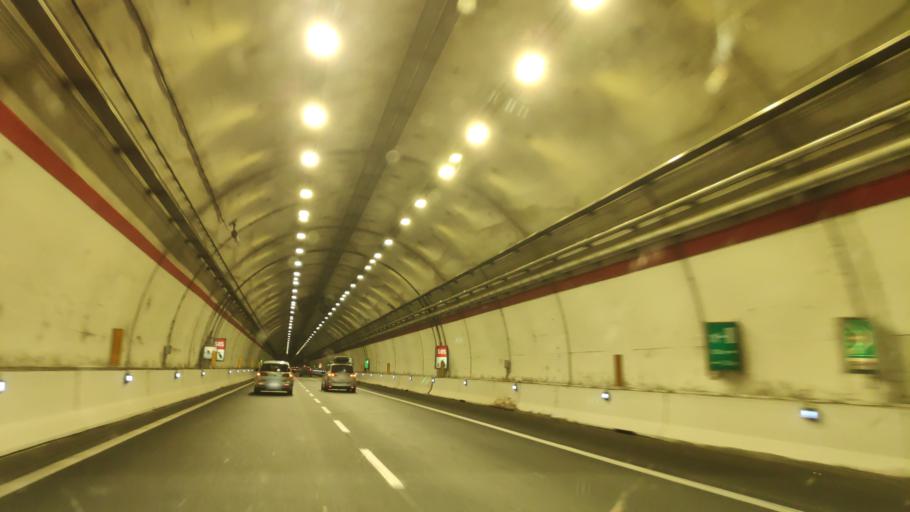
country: IT
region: Campania
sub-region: Provincia di Salerno
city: Petina
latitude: 40.5661
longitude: 15.3736
